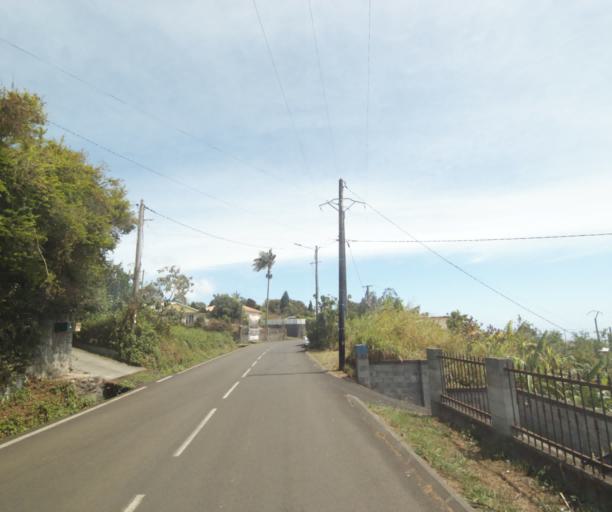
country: RE
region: Reunion
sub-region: Reunion
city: Trois-Bassins
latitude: -21.0634
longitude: 55.3081
